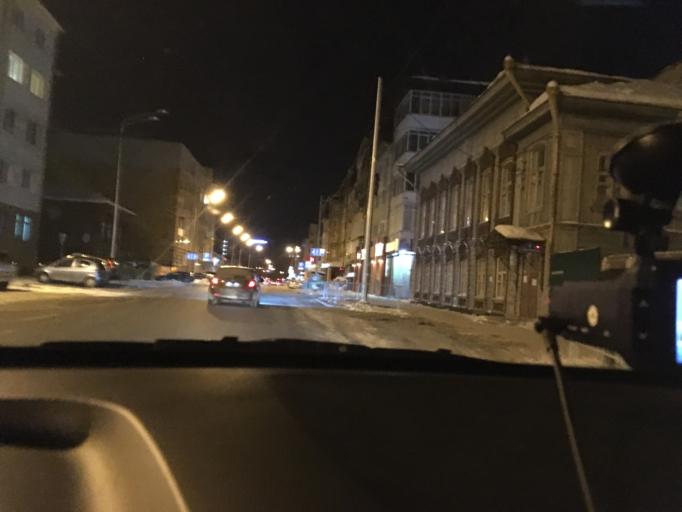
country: RU
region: Tjumen
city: Tyumen
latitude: 57.1589
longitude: 65.5418
